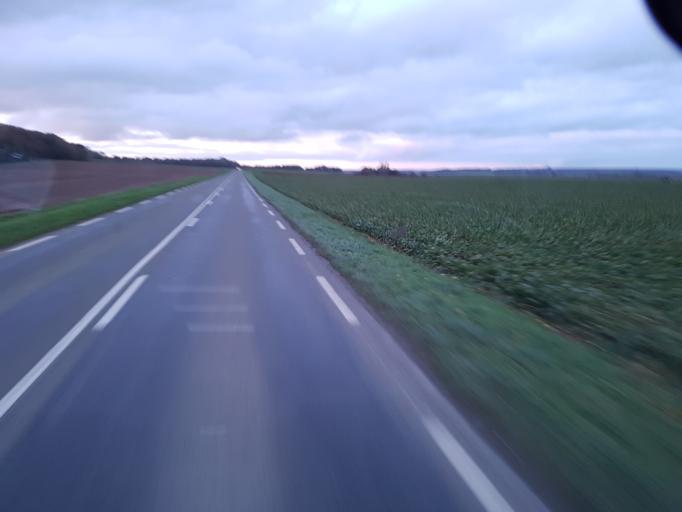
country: FR
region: Picardie
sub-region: Departement de l'Aisne
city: Coincy
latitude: 49.1603
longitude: 3.3824
